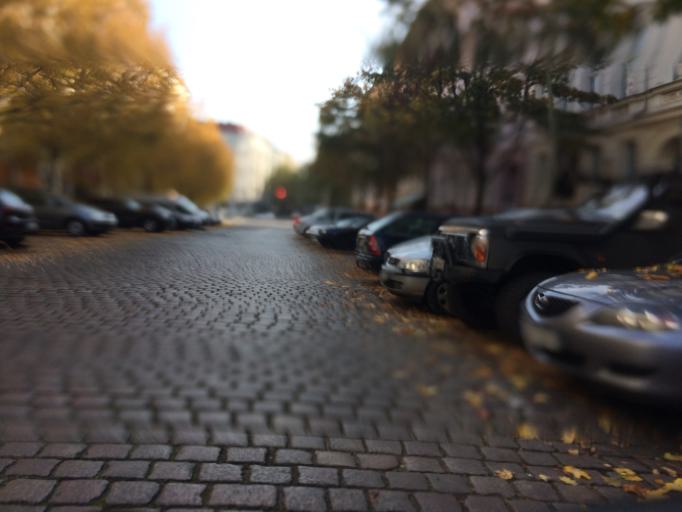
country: DE
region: Berlin
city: Prenzlauer Berg Bezirk
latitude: 52.5336
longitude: 13.4278
